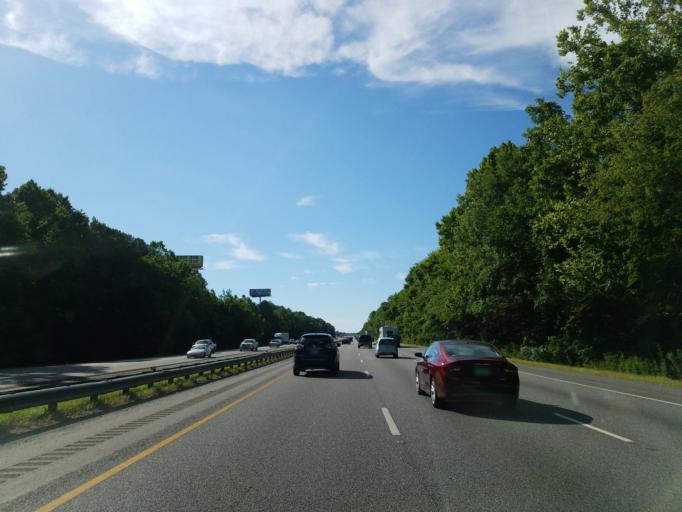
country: US
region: Georgia
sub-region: Bartow County
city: Cartersville
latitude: 34.2604
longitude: -84.7998
